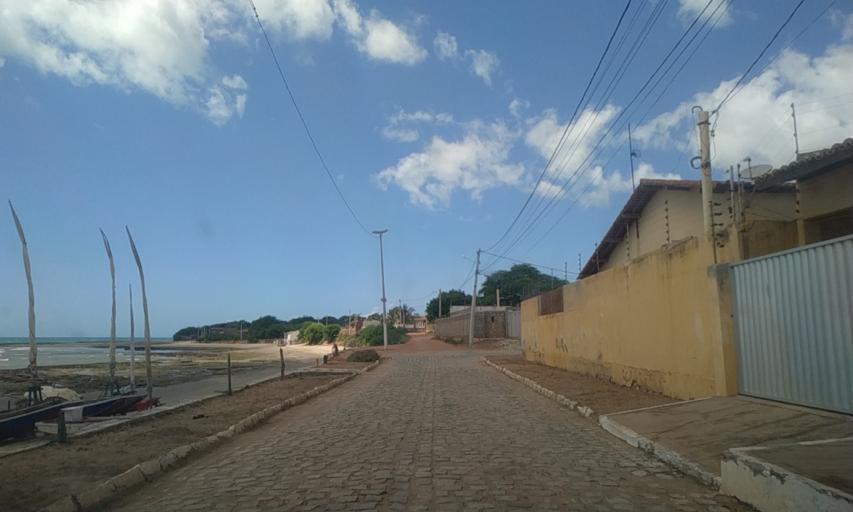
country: BR
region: Rio Grande do Norte
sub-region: Areia Branca
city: Areia Branca
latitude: -4.9256
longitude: -37.1112
